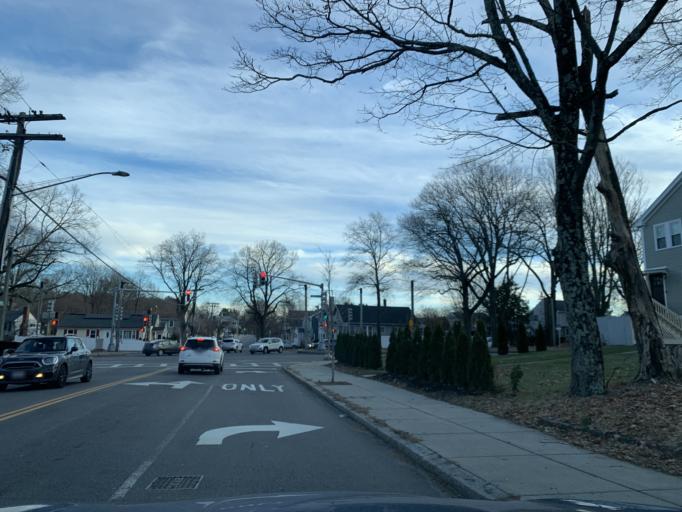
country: US
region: Massachusetts
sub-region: Norfolk County
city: Dedham
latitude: 42.2910
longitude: -71.1687
